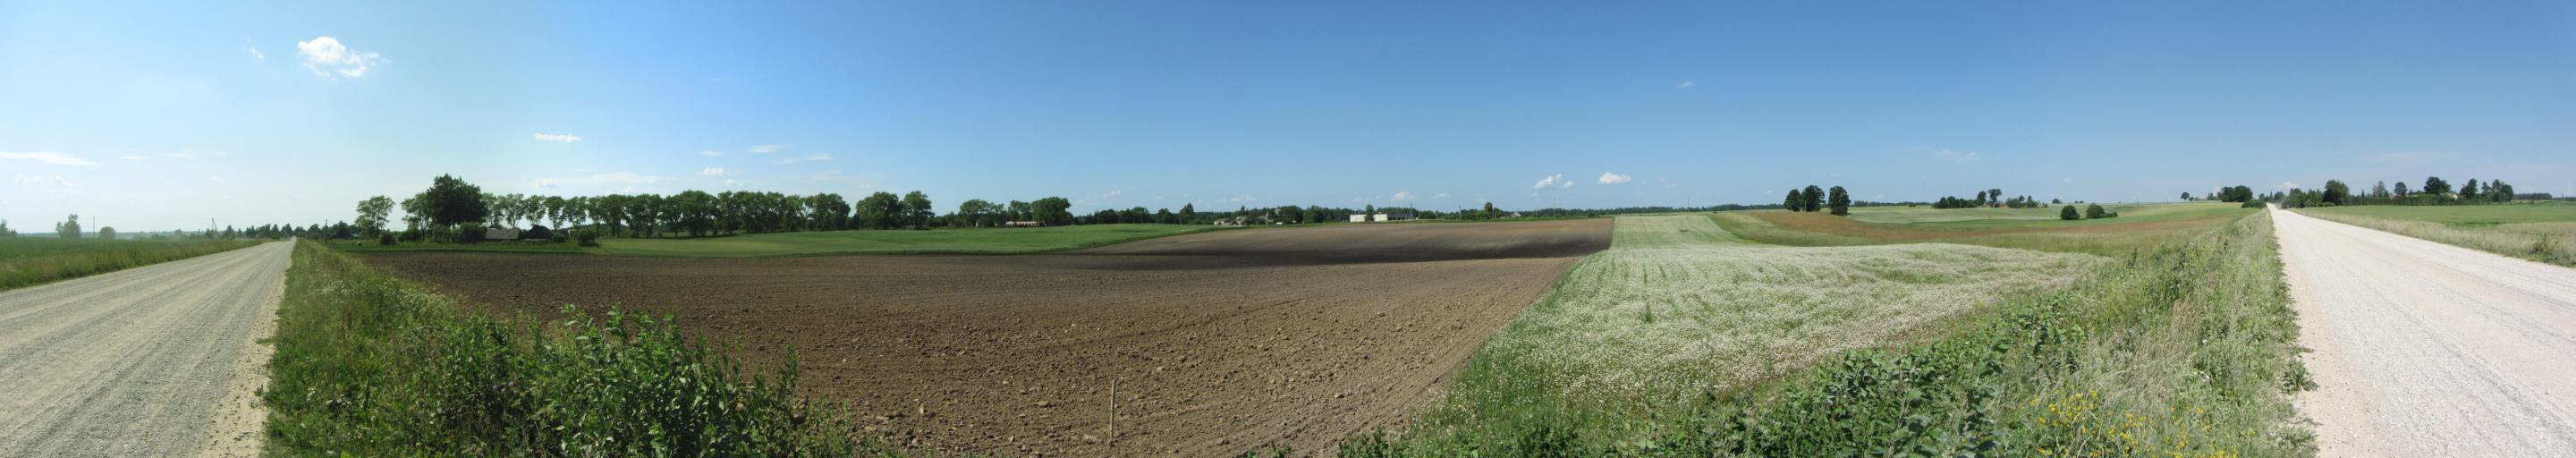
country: LT
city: Sirvintos
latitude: 55.2791
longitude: 25.0273
